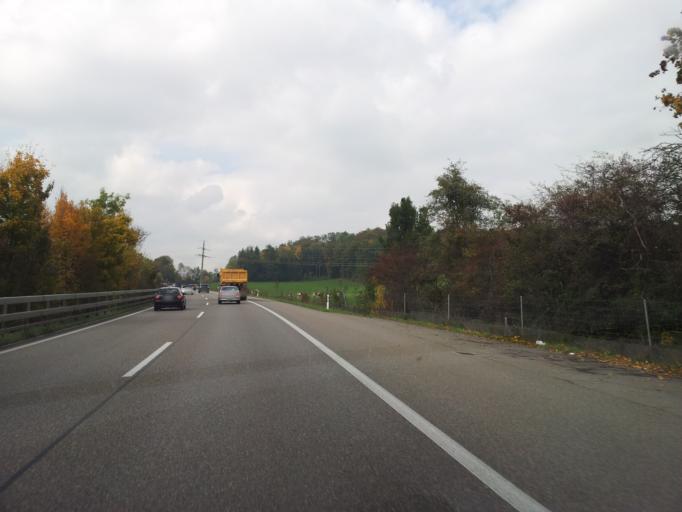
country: CH
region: Bern
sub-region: Bern-Mittelland District
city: Rubigen
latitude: 46.9036
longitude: 7.5291
